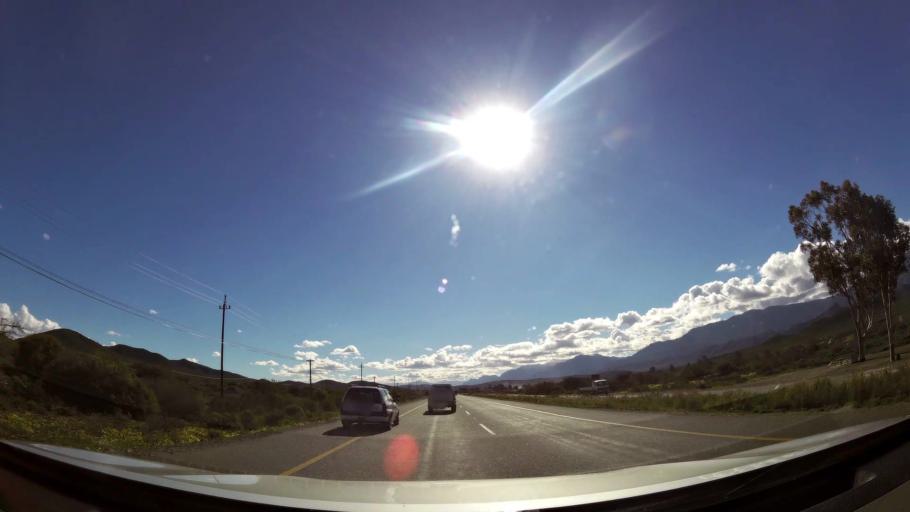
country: ZA
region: Western Cape
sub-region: Cape Winelands District Municipality
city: Ashton
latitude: -33.7733
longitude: 19.7535
